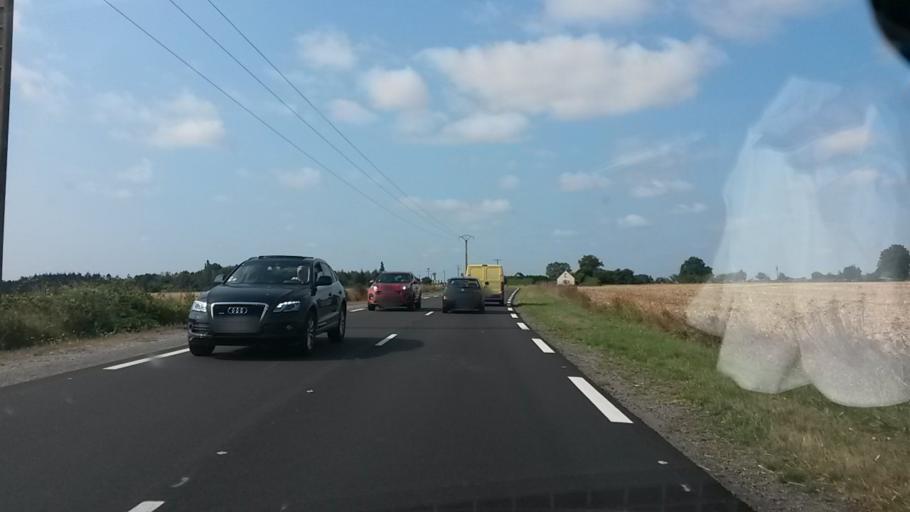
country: FR
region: Haute-Normandie
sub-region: Departement de l'Eure
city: Verneuil-sur-Avre
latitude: 48.7807
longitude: 0.9763
